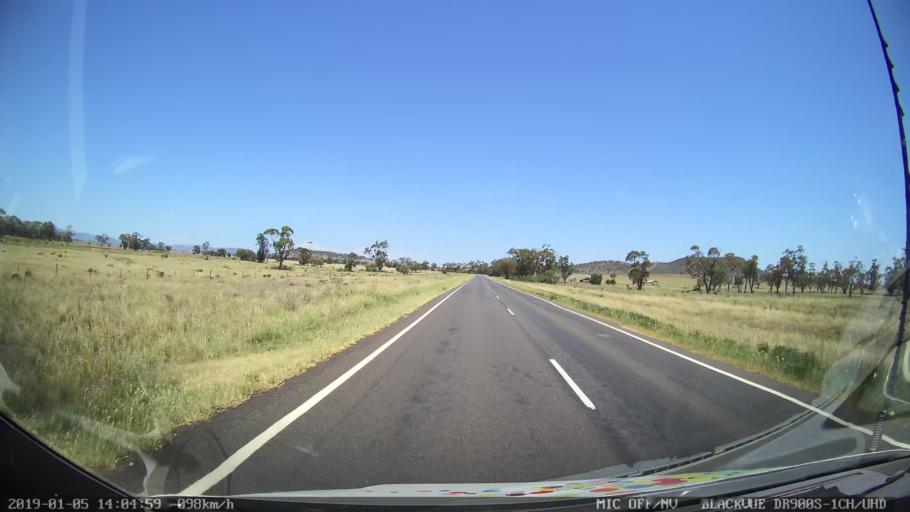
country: AU
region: New South Wales
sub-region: Gunnedah
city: Gunnedah
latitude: -31.2056
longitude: 150.3702
